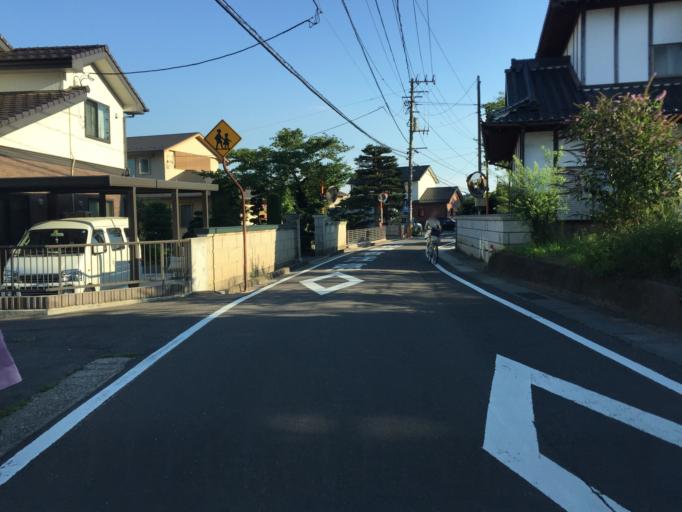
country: JP
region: Fukushima
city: Hobaramachi
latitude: 37.8656
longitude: 140.5228
